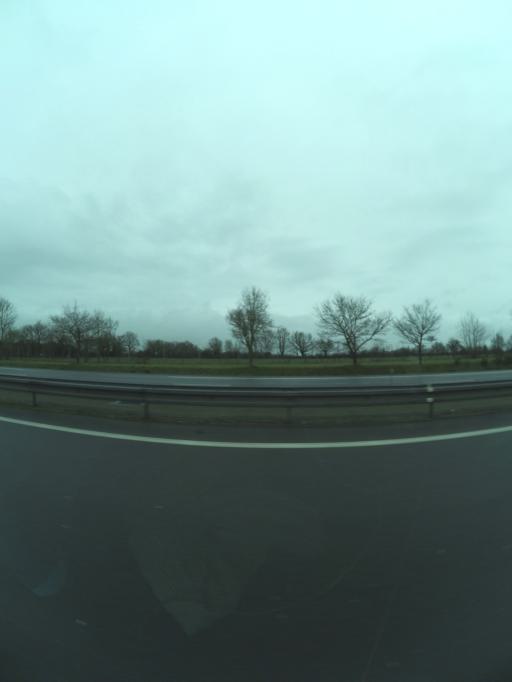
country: FR
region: Pays de la Loire
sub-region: Departement de Maine-et-Loire
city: Ingrandes
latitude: 47.4282
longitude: -0.9221
